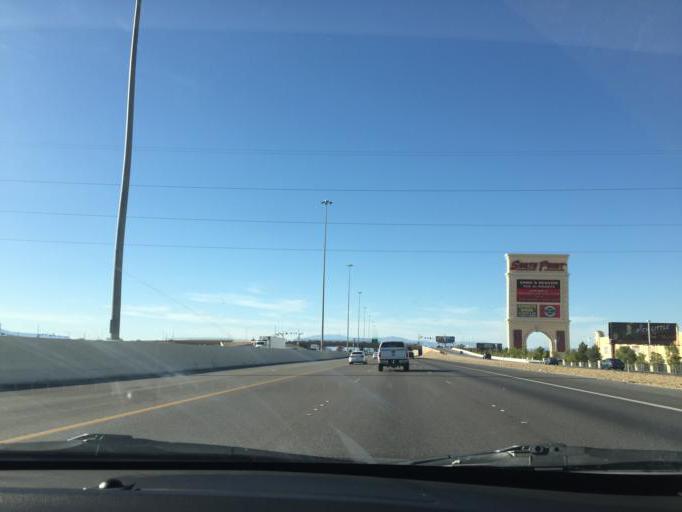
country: US
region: Nevada
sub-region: Clark County
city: Enterprise
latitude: 36.0093
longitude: -115.1801
